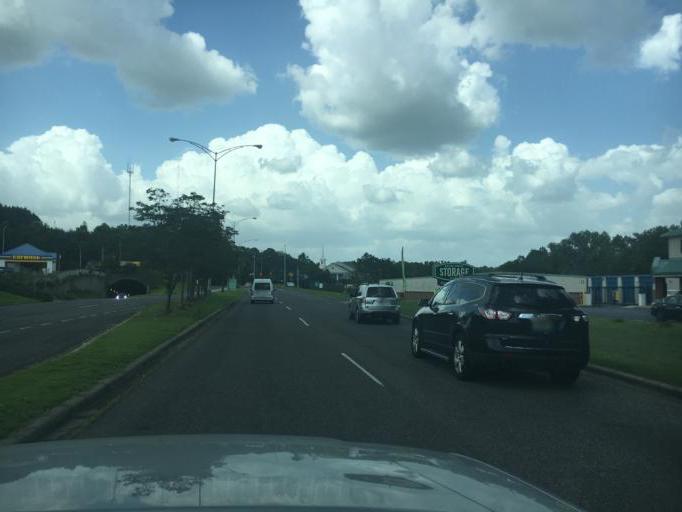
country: US
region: Alabama
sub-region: Jefferson County
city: Homewood
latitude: 33.4695
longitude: -86.8180
